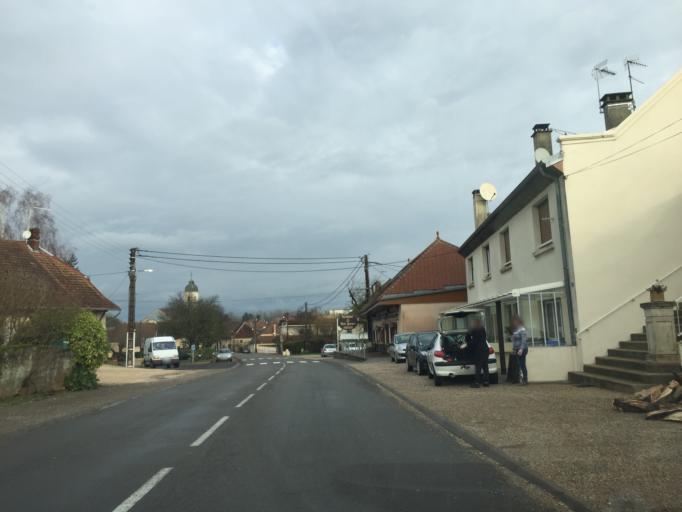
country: FR
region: Franche-Comte
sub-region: Departement du Jura
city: Mont-sous-Vaudrey
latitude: 46.9762
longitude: 5.6038
